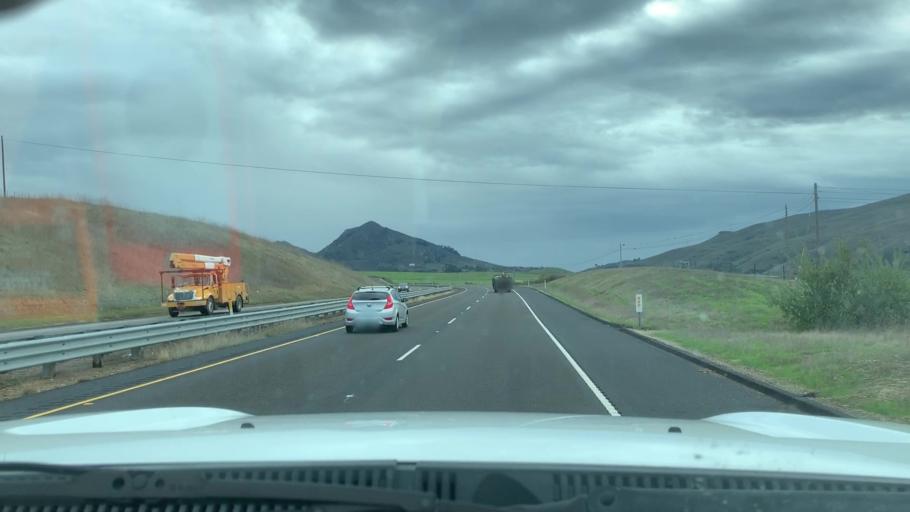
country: US
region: California
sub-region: San Luis Obispo County
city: Los Osos
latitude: 35.3393
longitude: -120.7612
